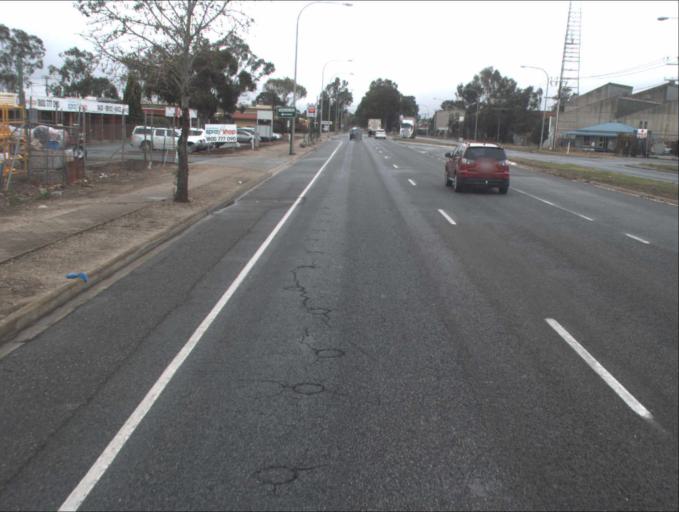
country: AU
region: South Australia
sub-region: Port Adelaide Enfield
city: Blair Athol
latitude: -34.8452
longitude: 138.5867
